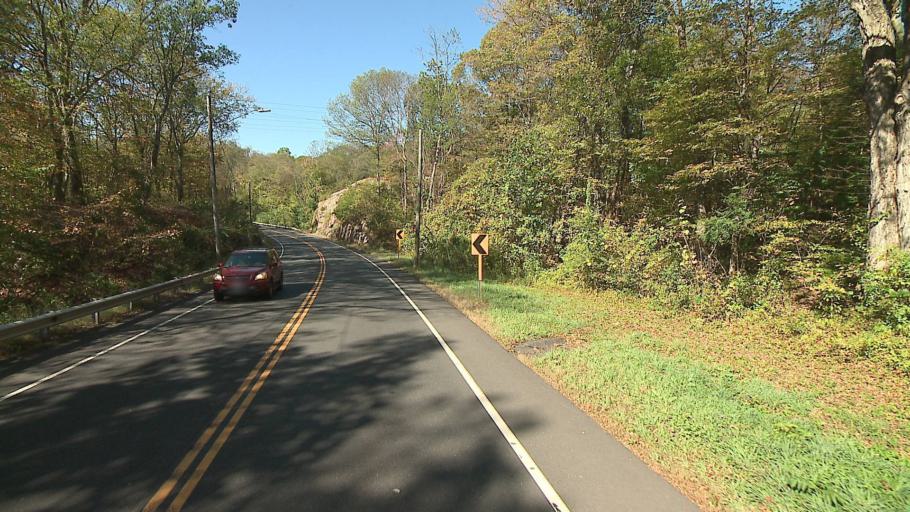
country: US
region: Connecticut
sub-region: Middlesex County
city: Higganum
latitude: 41.5614
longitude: -72.5749
